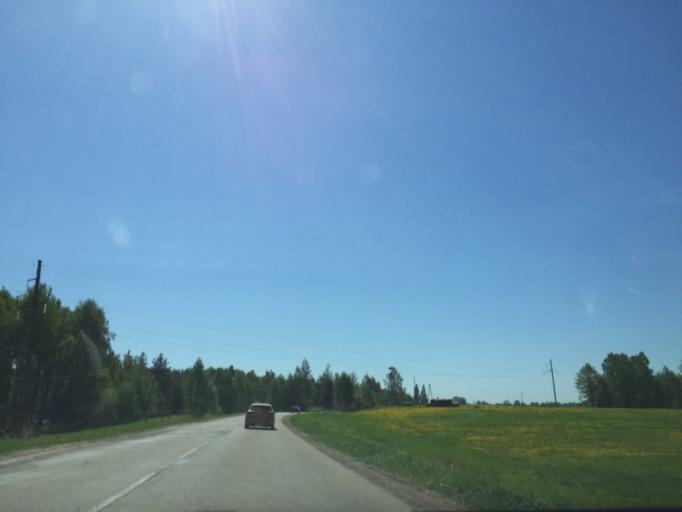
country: LV
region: Malpils
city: Malpils
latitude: 56.9274
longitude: 24.9367
